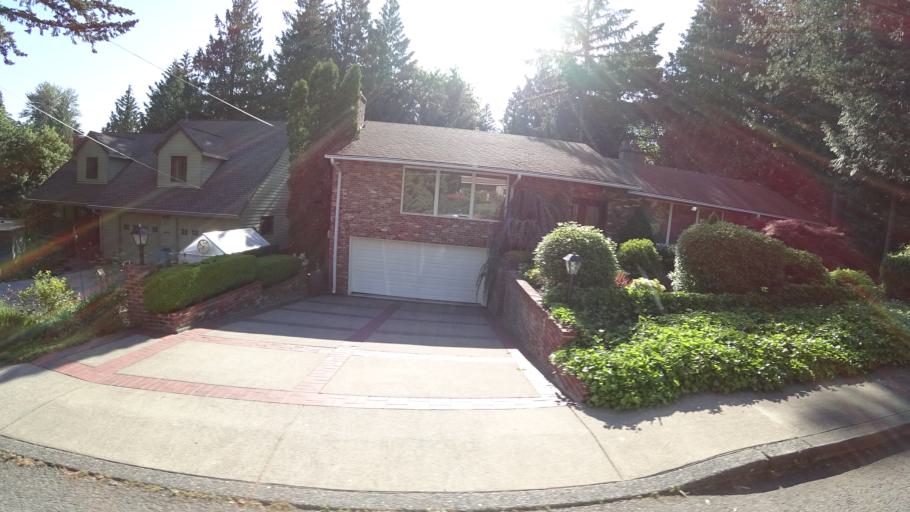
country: US
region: Oregon
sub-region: Clackamas County
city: Happy Valley
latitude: 45.4707
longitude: -122.5401
